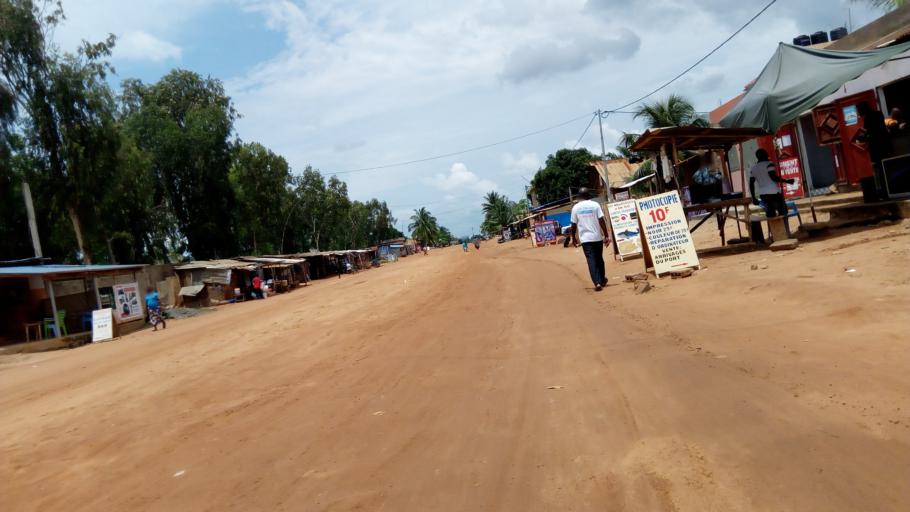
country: TG
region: Maritime
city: Lome
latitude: 6.2261
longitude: 1.1603
